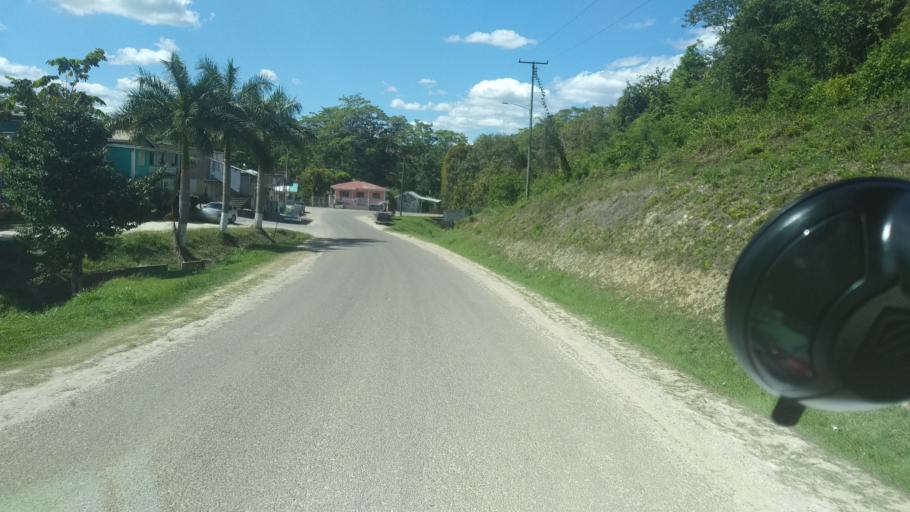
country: BZ
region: Cayo
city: Benque Viejo del Carmen
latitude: 17.0779
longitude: -89.1359
